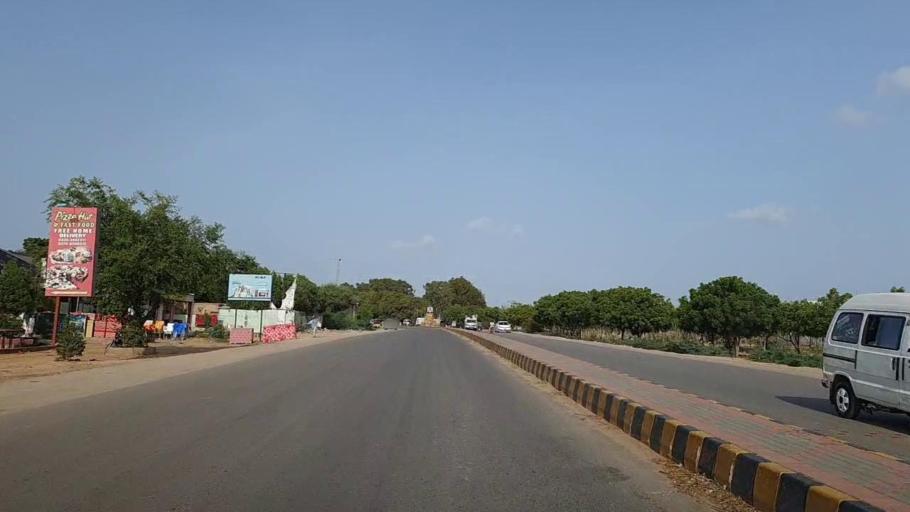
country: PK
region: Sindh
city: Thatta
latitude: 24.7437
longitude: 67.8882
